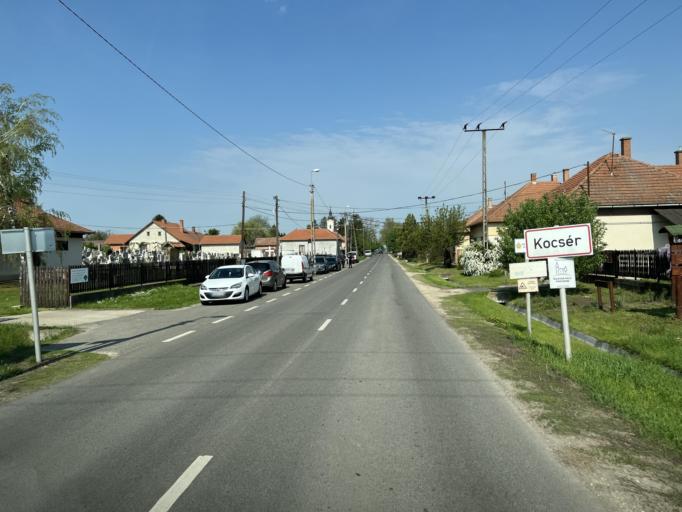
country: HU
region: Pest
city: Kocser
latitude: 47.0007
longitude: 19.9272
